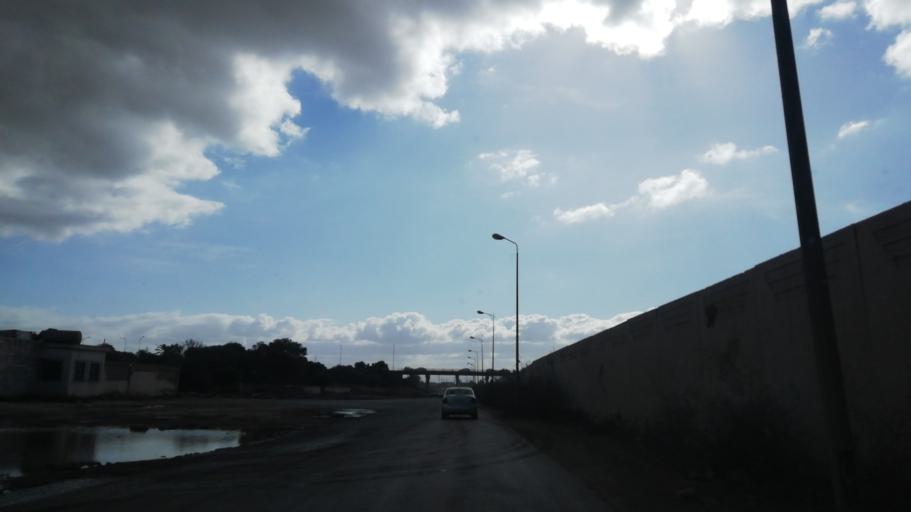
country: DZ
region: Oran
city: Es Senia
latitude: 35.6257
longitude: -0.5903
